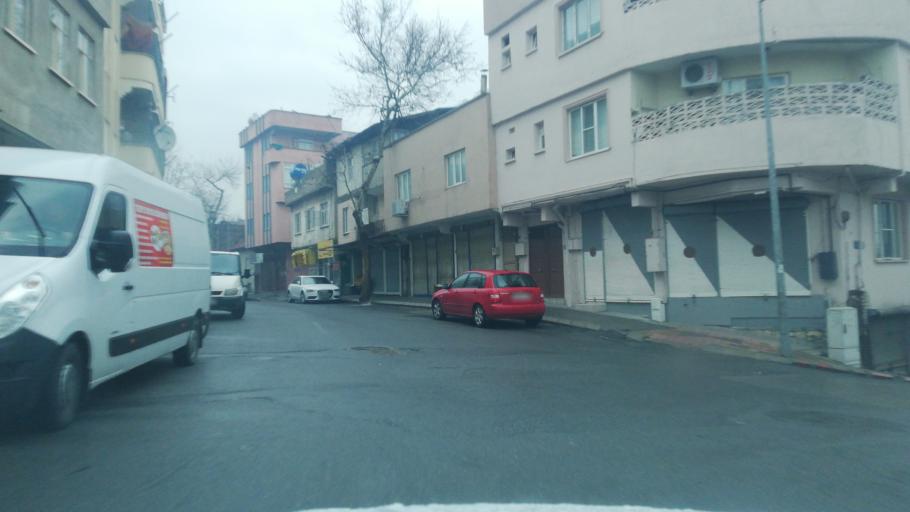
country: TR
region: Kahramanmaras
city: Kahramanmaras
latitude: 37.5812
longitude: 36.9364
